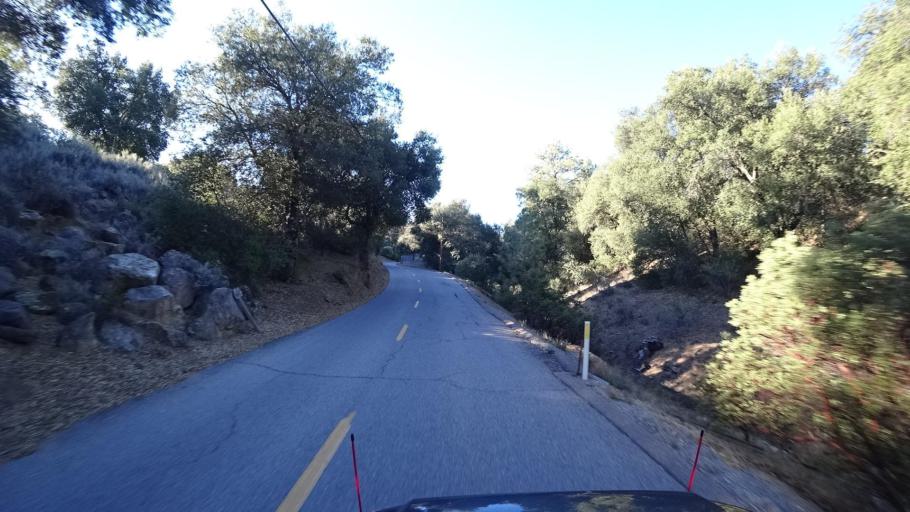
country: US
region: California
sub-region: San Diego County
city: Pine Valley
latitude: 32.8214
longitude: -116.5377
